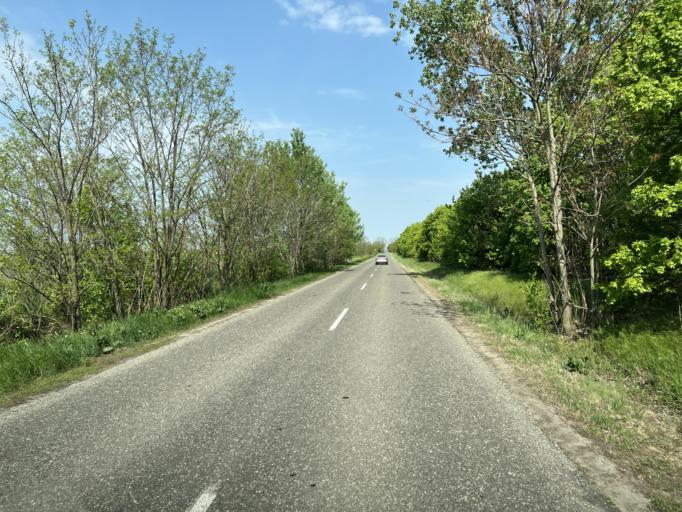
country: HU
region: Pest
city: Tortel
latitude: 47.1108
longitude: 19.9795
